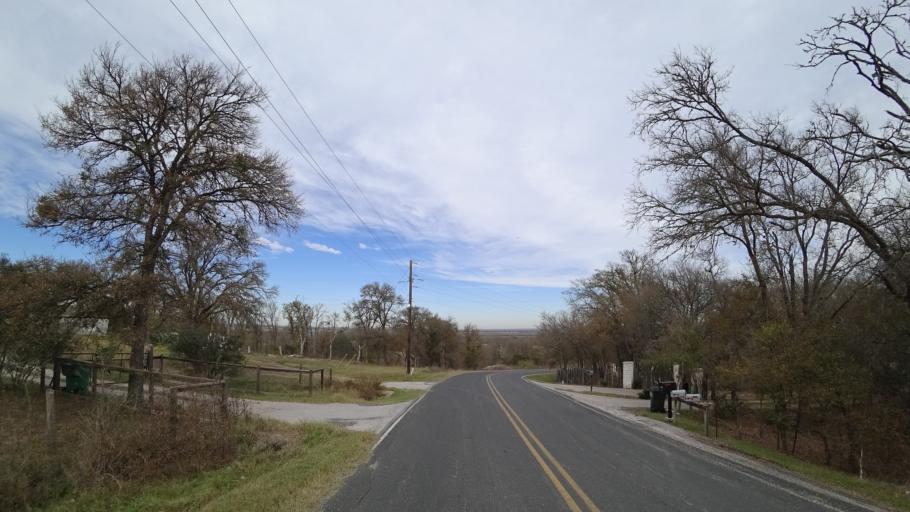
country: US
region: Texas
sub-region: Travis County
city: Garfield
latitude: 30.1451
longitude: -97.5868
